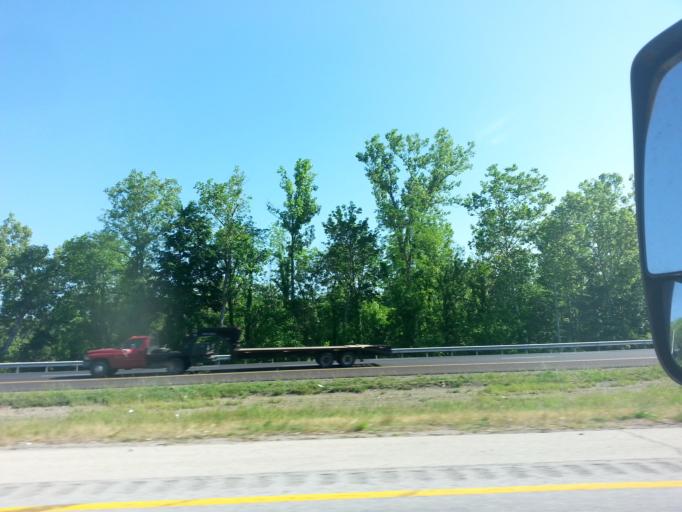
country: US
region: Kentucky
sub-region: Jefferson County
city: Middletown
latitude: 38.2232
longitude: -85.5234
